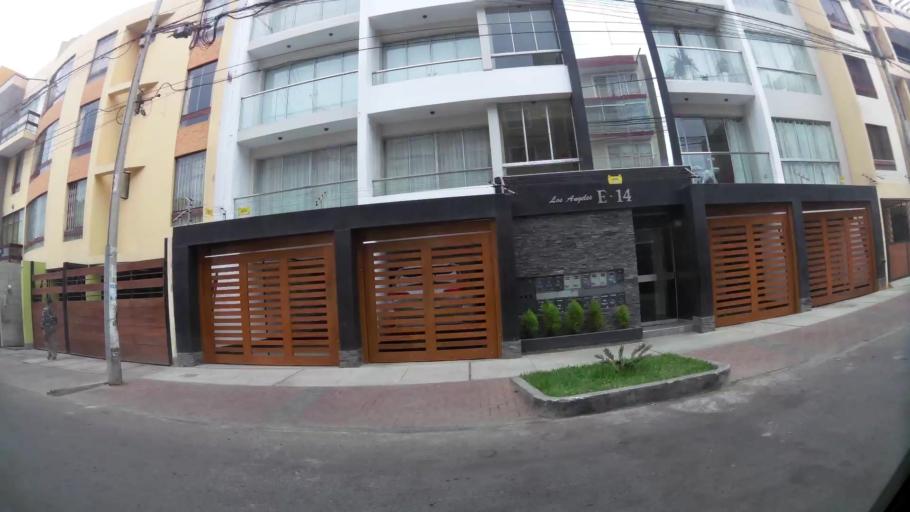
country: PE
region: La Libertad
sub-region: Provincia de Trujillo
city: Buenos Aires
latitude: -8.1358
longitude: -79.0389
